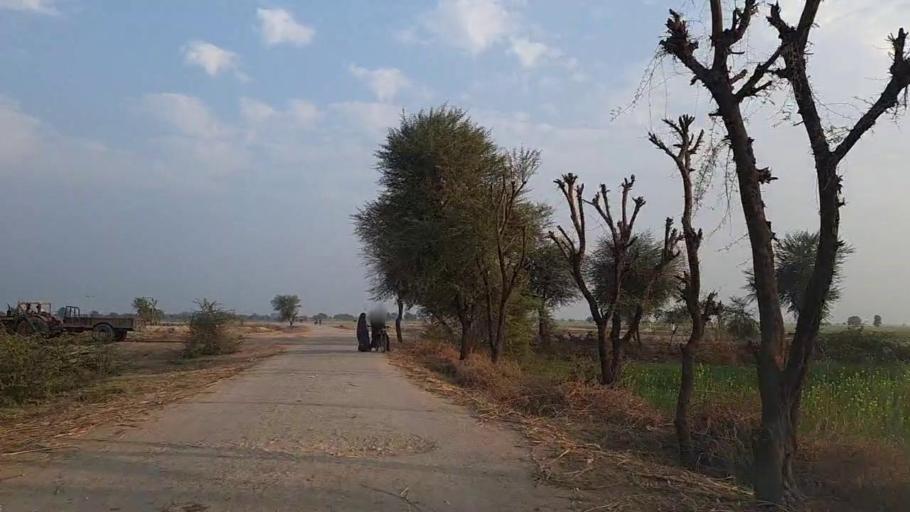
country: PK
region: Sindh
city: Samaro
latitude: 25.2971
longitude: 69.2245
